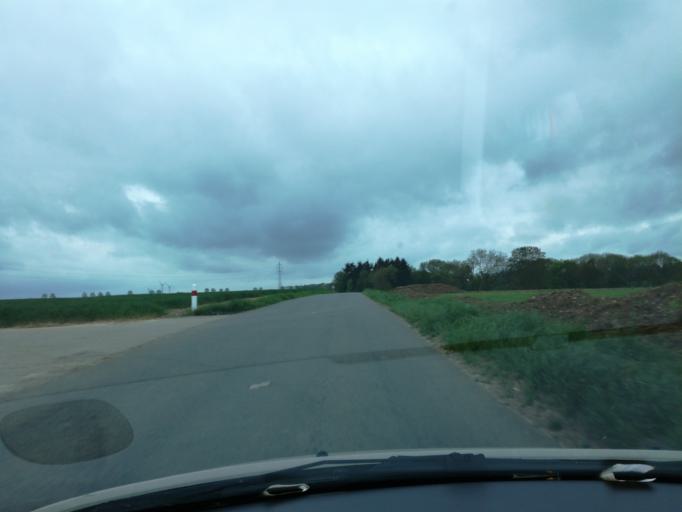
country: FR
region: Picardie
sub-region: Departement de la Somme
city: Poix-de-Picardie
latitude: 49.8166
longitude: 1.9856
